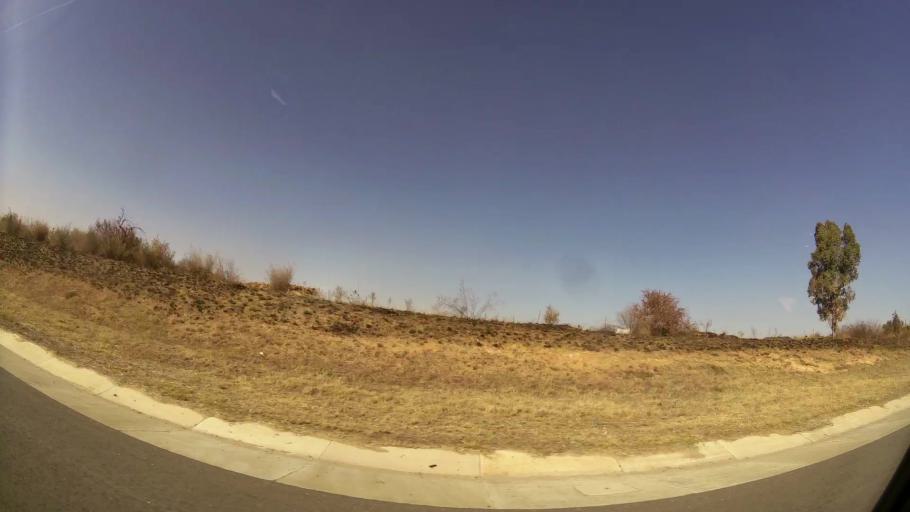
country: ZA
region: Gauteng
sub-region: City of Johannesburg Metropolitan Municipality
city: Diepsloot
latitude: -25.9517
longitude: 27.9557
